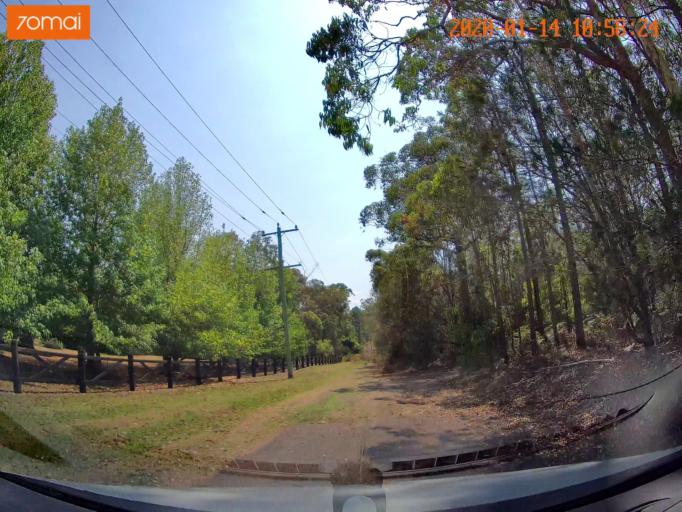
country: AU
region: New South Wales
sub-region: Lake Macquarie Shire
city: Dora Creek
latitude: -33.0993
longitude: 151.4914
